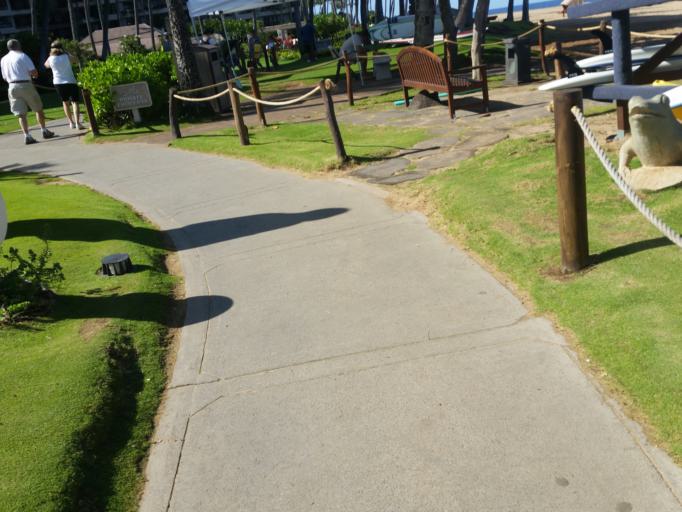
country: US
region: Hawaii
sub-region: Maui County
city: Ka'anapali
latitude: 20.9192
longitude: -156.6962
